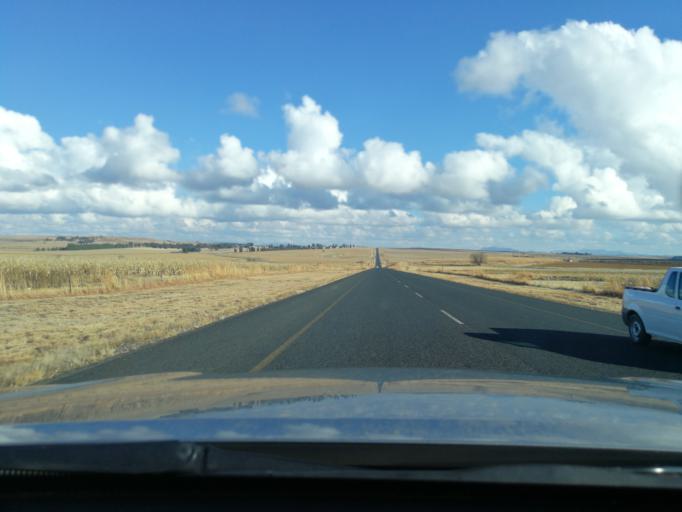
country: ZA
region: Orange Free State
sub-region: Thabo Mofutsanyana District Municipality
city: Bethlehem
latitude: -28.0929
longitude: 28.3538
